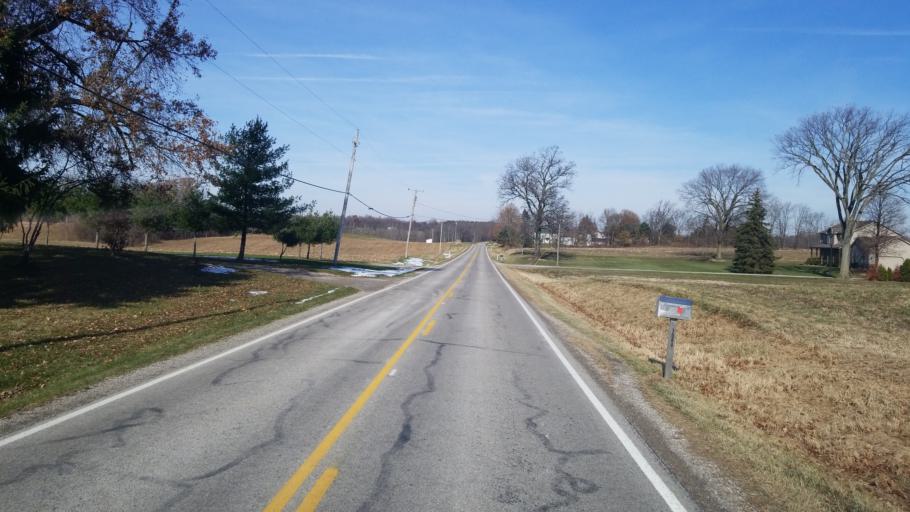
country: US
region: Ohio
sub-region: Huron County
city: Willard
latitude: 41.1091
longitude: -82.6860
